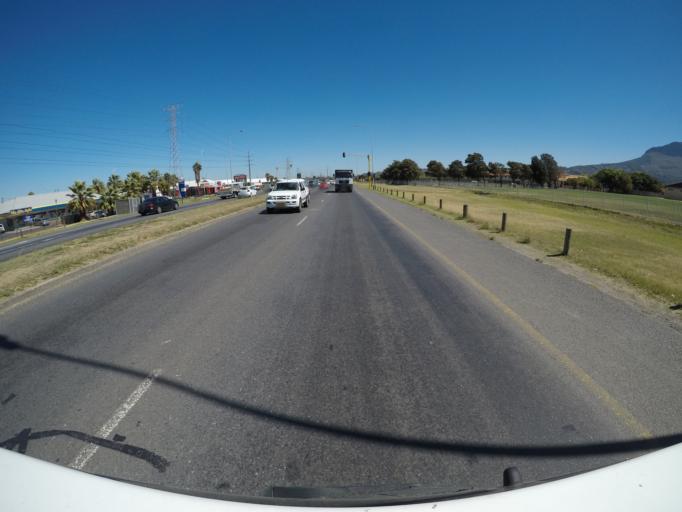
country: ZA
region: Western Cape
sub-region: Cape Winelands District Municipality
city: Stellenbosch
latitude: -34.0951
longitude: 18.8456
